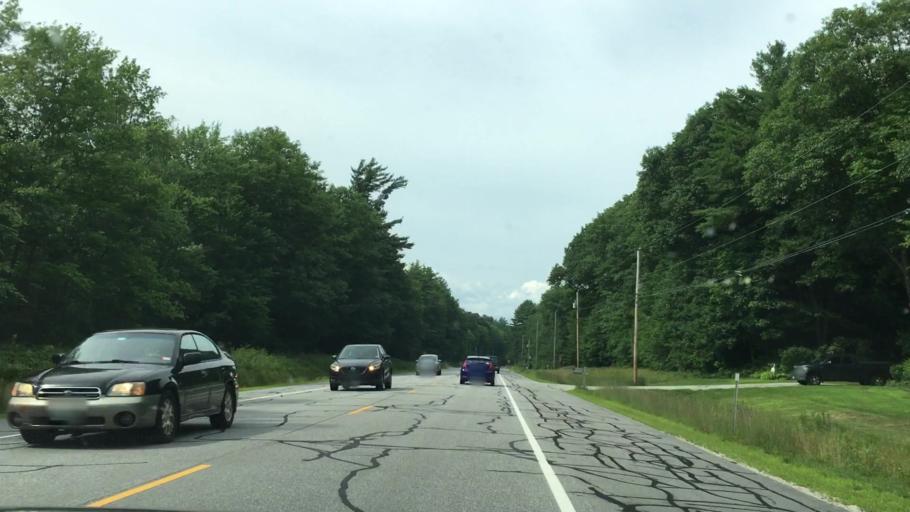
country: US
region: New Hampshire
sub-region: Hillsborough County
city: Hillsborough
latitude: 43.0876
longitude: -71.9188
